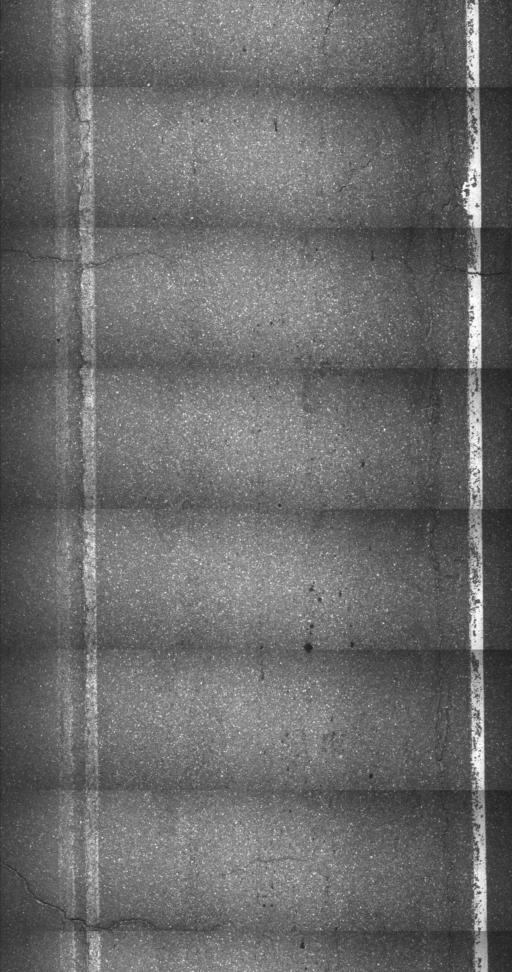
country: US
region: Vermont
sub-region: Caledonia County
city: Hardwick
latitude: 44.4672
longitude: -72.2715
